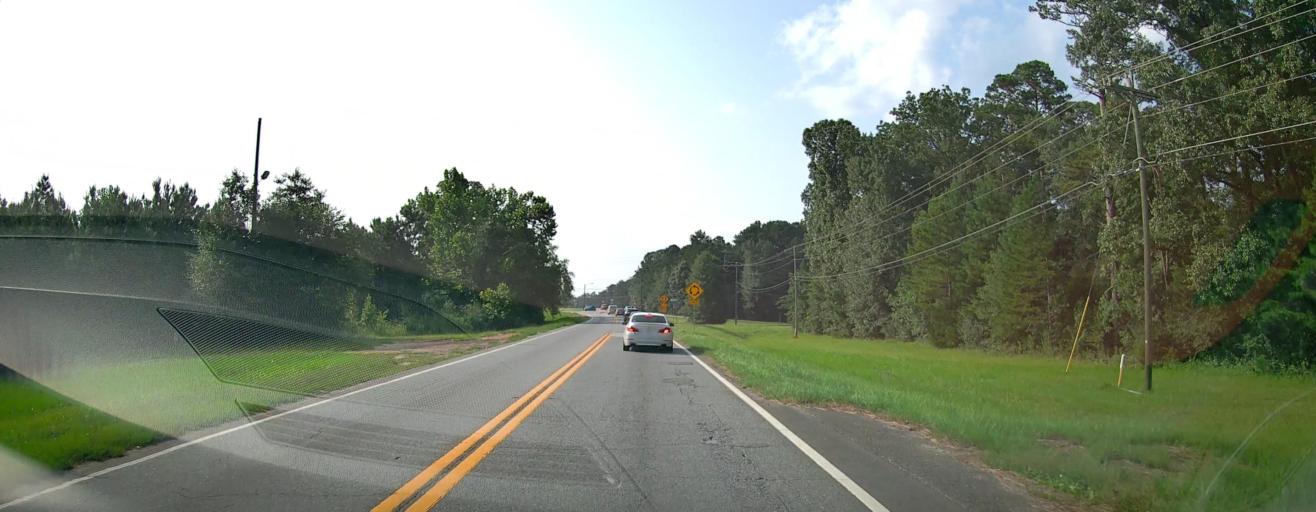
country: US
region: Georgia
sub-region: Bibb County
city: Macon
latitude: 32.9348
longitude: -83.7163
